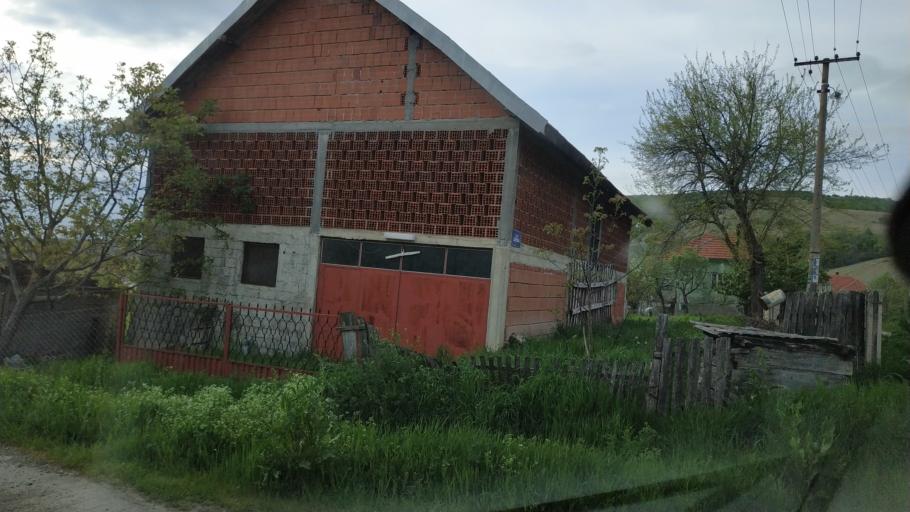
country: RS
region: Central Serbia
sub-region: Zajecarski Okrug
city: Soko Banja
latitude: 43.5242
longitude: 21.8622
